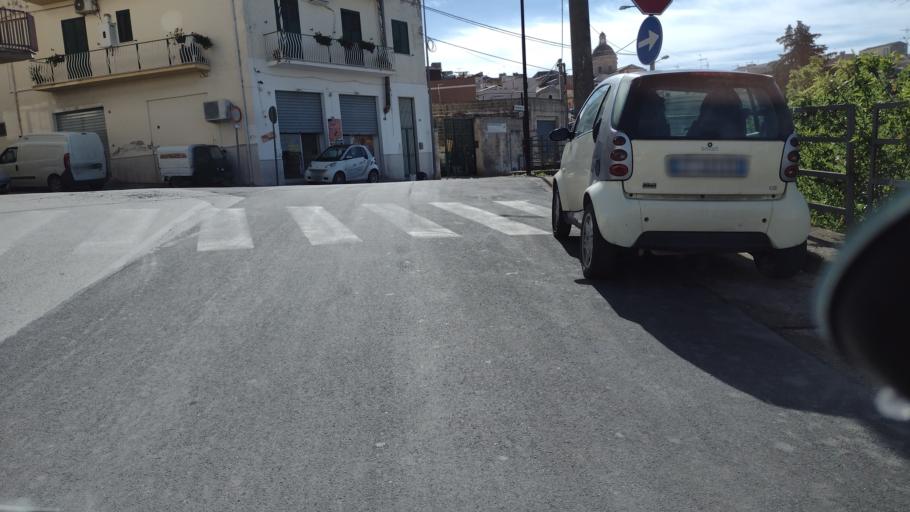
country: IT
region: Sicily
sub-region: Provincia di Siracusa
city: Noto
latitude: 36.8967
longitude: 15.0698
